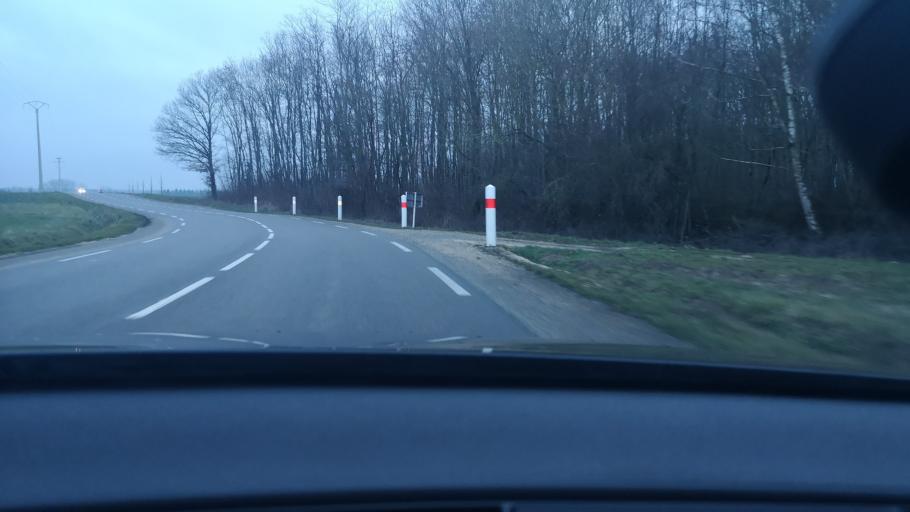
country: FR
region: Bourgogne
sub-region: Departement de la Cote-d'Or
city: Seurre
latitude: 47.0591
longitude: 5.0911
